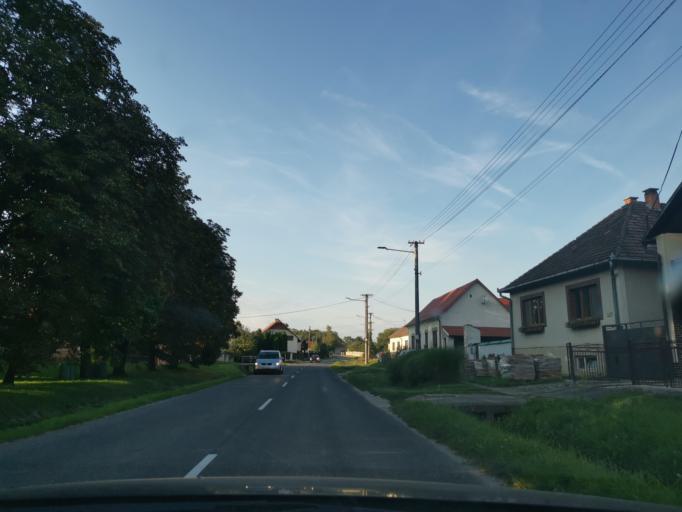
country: SK
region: Trnavsky
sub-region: Okres Senica
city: Senica
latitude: 48.6792
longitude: 17.2578
